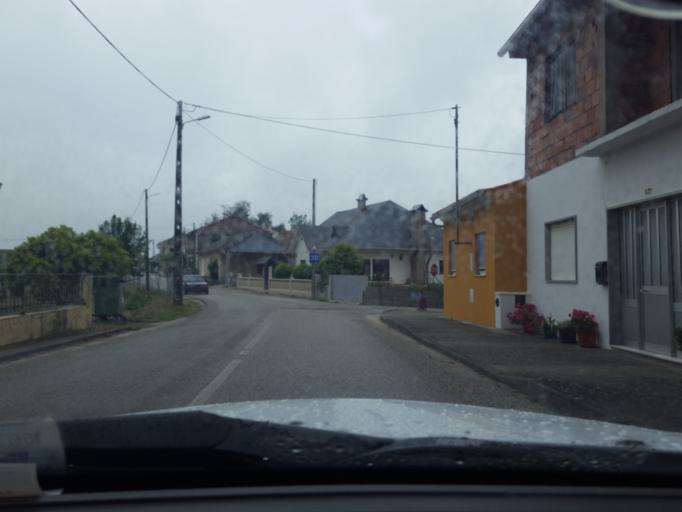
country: PT
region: Leiria
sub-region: Leiria
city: Caranguejeira
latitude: 39.7942
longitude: -8.7523
